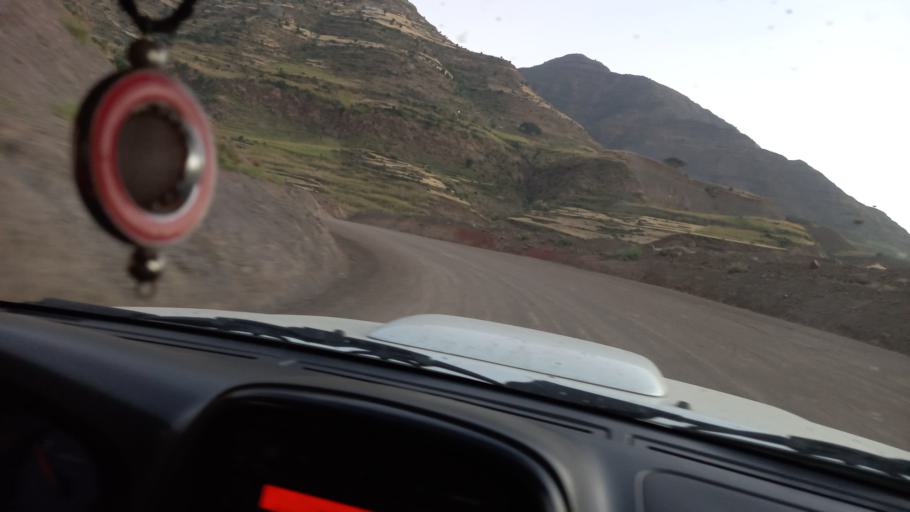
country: ET
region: Amhara
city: Debark'
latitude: 13.0326
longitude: 38.0535
